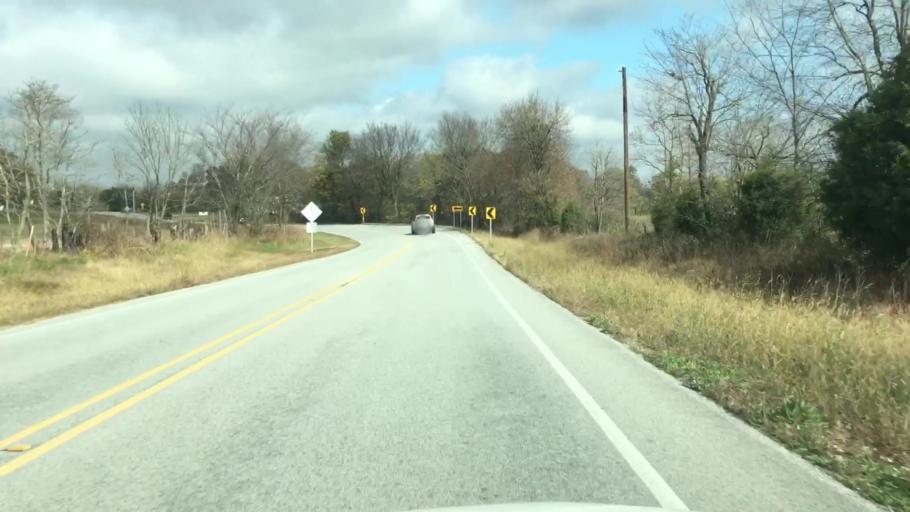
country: US
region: Arkansas
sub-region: Benton County
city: Centerton
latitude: 36.2951
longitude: -94.3415
